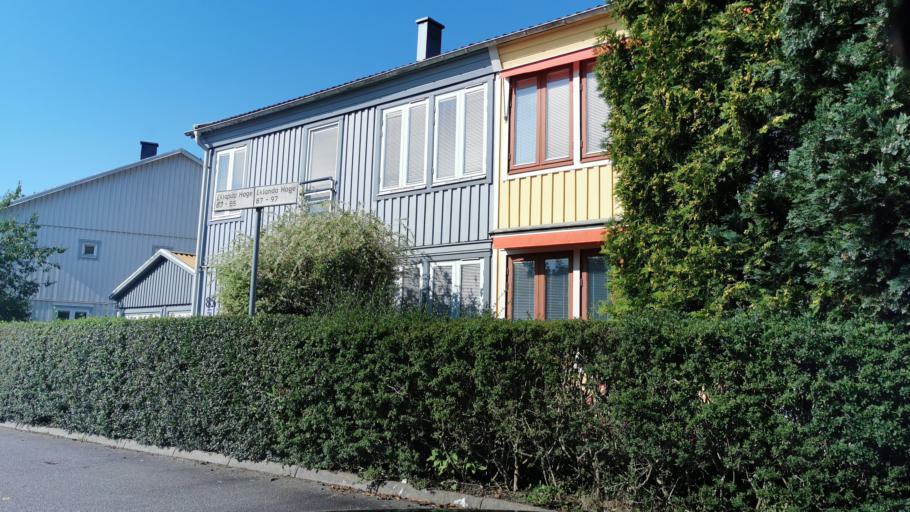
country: SE
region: Vaestra Goetaland
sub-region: Goteborg
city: Goeteborg
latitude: 57.6570
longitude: 11.9618
